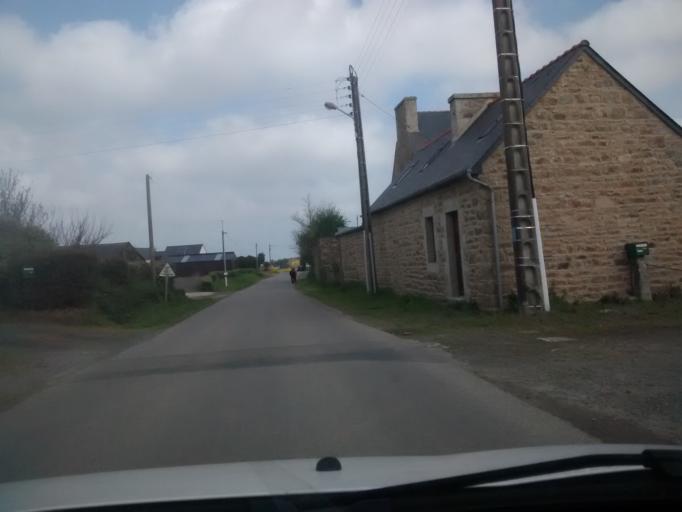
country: FR
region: Brittany
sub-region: Departement des Cotes-d'Armor
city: Penvenan
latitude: 48.8162
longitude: -3.3025
